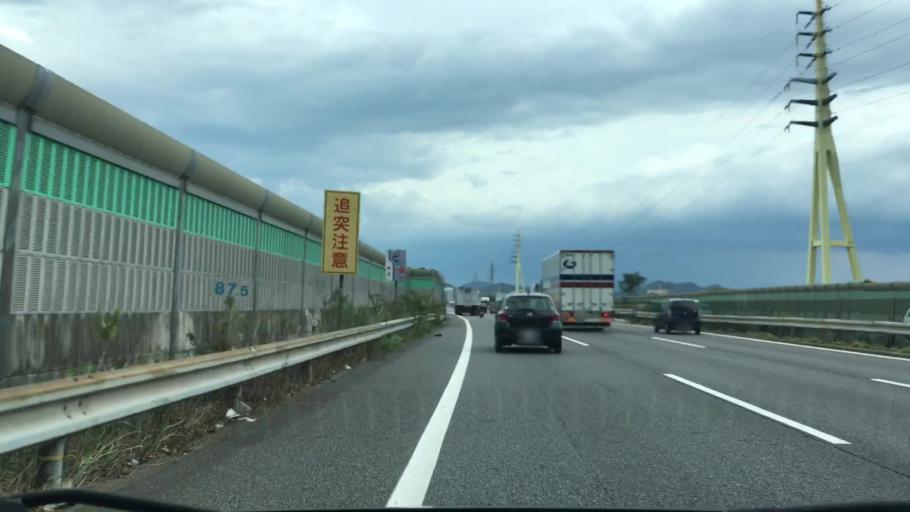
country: JP
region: Hyogo
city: Himeji
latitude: 34.8057
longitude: 134.7015
